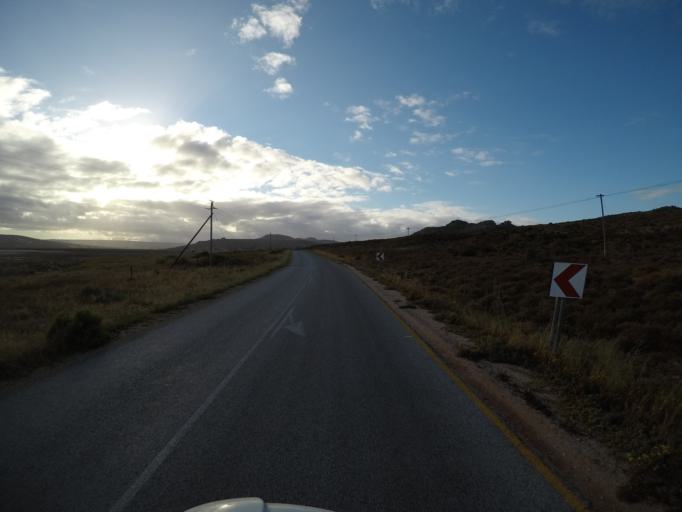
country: ZA
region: Western Cape
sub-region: West Coast District Municipality
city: Clanwilliam
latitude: -32.3242
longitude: 18.3620
